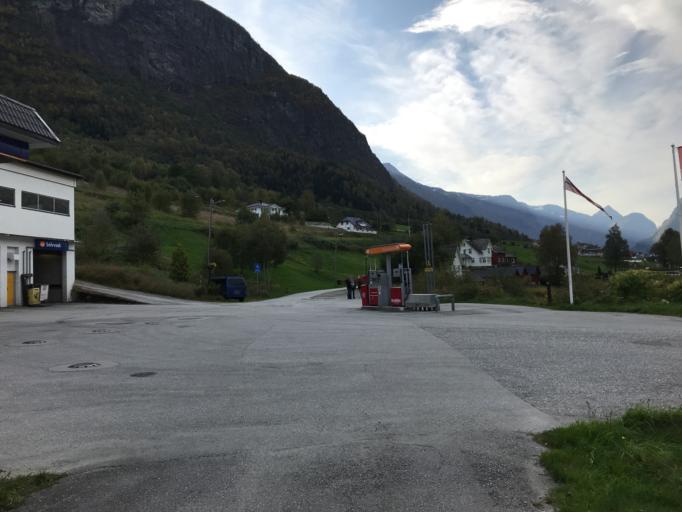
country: NO
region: Sogn og Fjordane
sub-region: Stryn
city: Stryn
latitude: 61.8417
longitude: 6.8109
